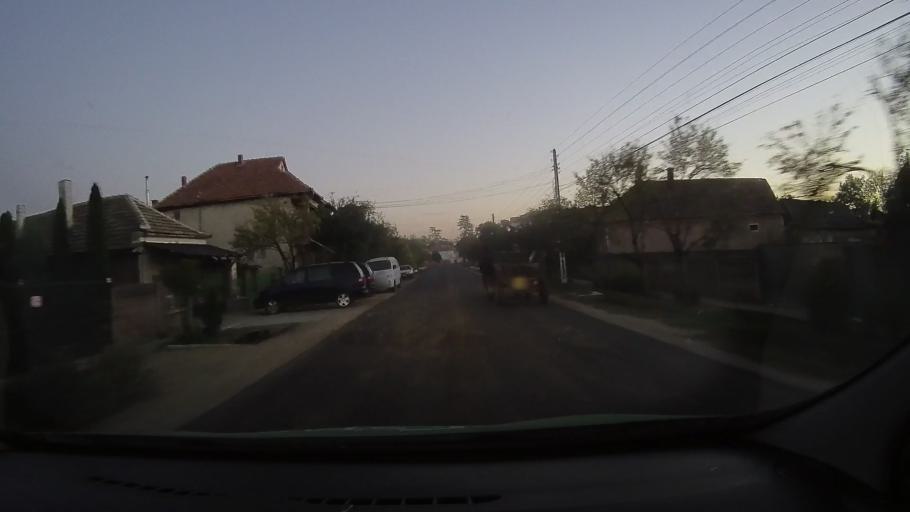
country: RO
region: Bihor
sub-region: Comuna Simian
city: Simian
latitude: 47.4999
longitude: 22.0910
